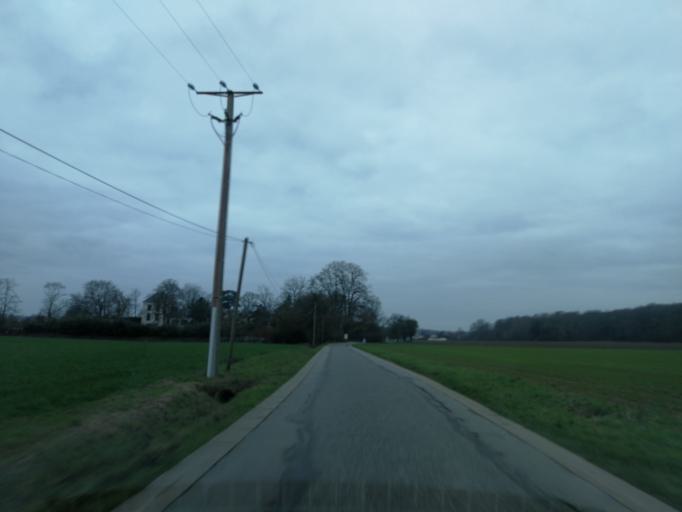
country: FR
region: Ile-de-France
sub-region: Departement de l'Essonne
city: Les Molieres
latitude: 48.6669
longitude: 2.0800
